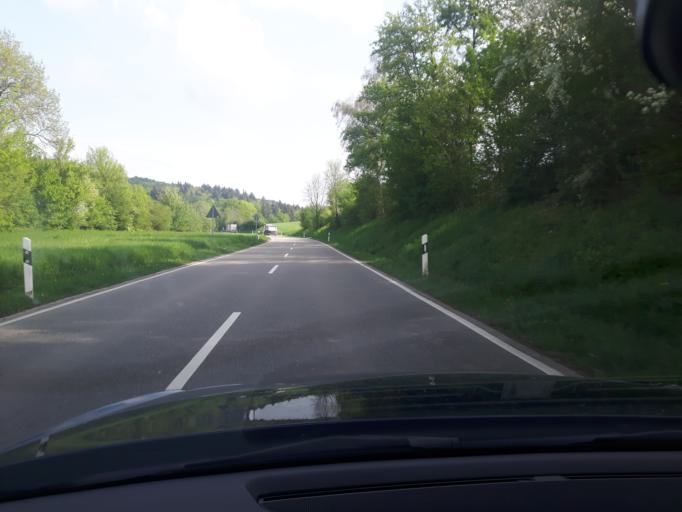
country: DE
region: Baden-Wuerttemberg
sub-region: Karlsruhe Region
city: Balzfeld
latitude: 49.2030
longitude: 8.8090
